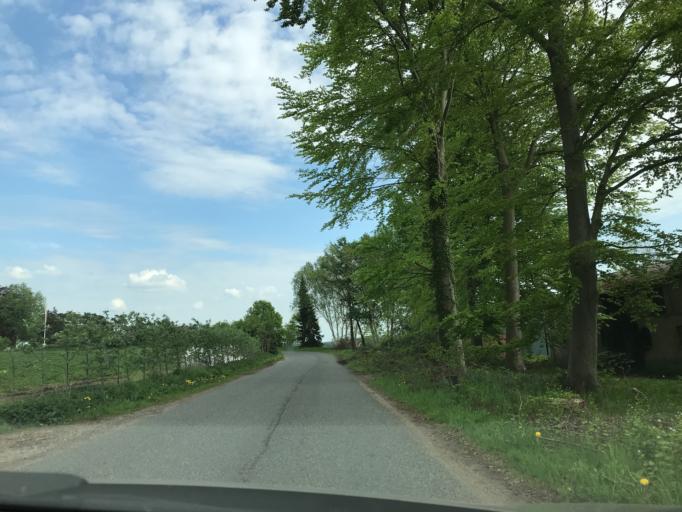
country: DK
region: South Denmark
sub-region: Assens Kommune
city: Assens
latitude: 55.3251
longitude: 9.9095
